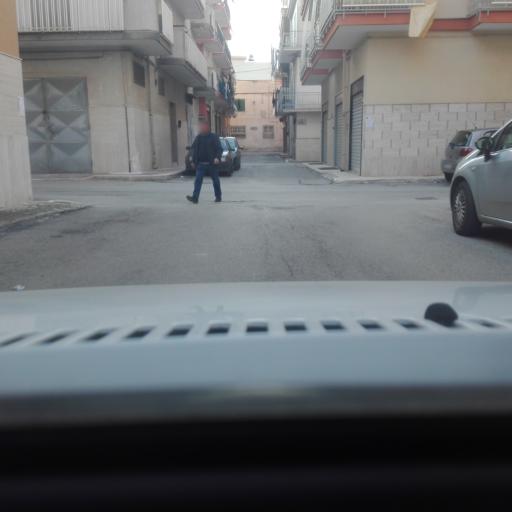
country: IT
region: Apulia
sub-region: Provincia di Bari
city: Corato
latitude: 41.1567
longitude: 16.4074
